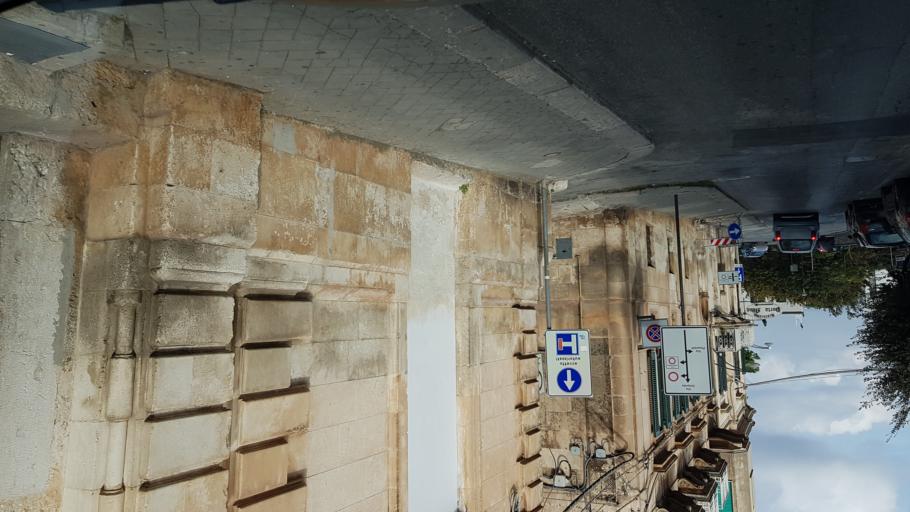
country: IT
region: Apulia
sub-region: Provincia di Brindisi
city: Ostuni
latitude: 40.7331
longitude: 17.5767
